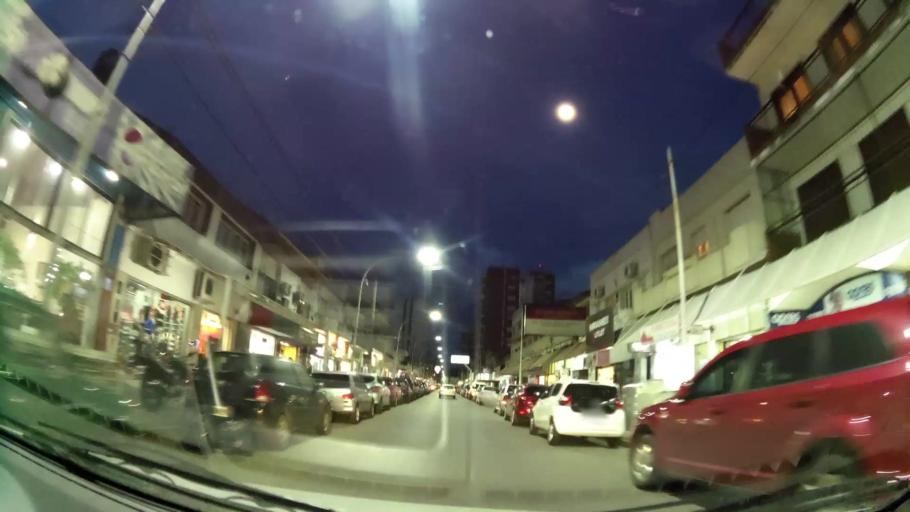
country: AR
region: Buenos Aires
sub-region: Partido de Quilmes
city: Quilmes
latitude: -34.7002
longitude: -58.3130
